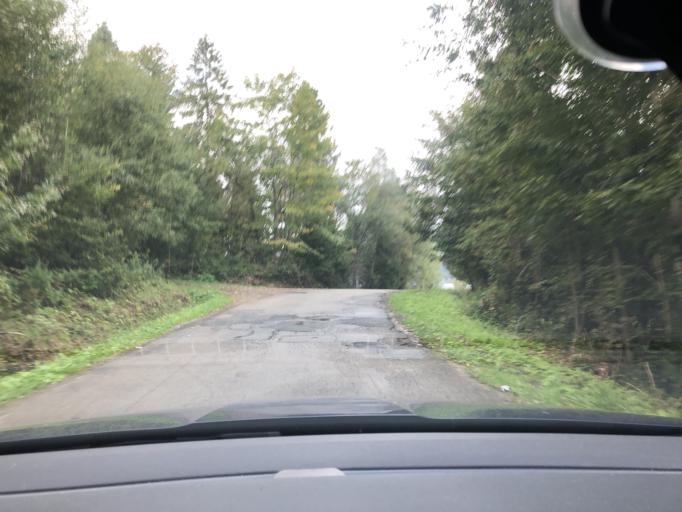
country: PL
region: Silesian Voivodeship
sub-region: Powiat zywiecki
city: Slemien
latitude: 49.7226
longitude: 19.4158
